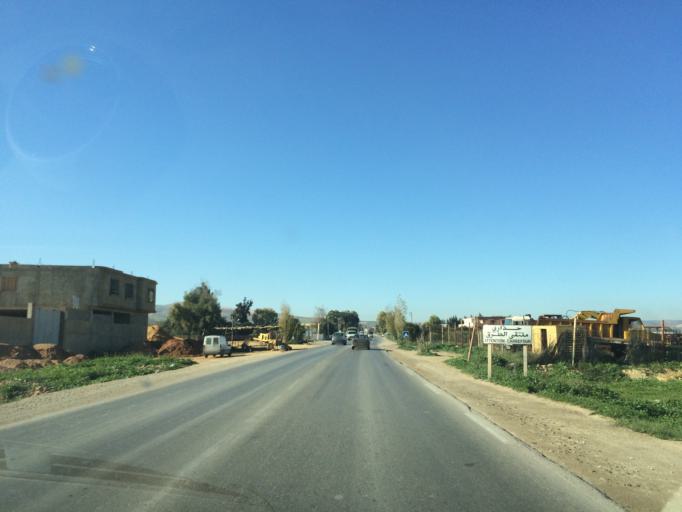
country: DZ
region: Relizane
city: Relizane
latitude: 35.9001
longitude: 0.5316
